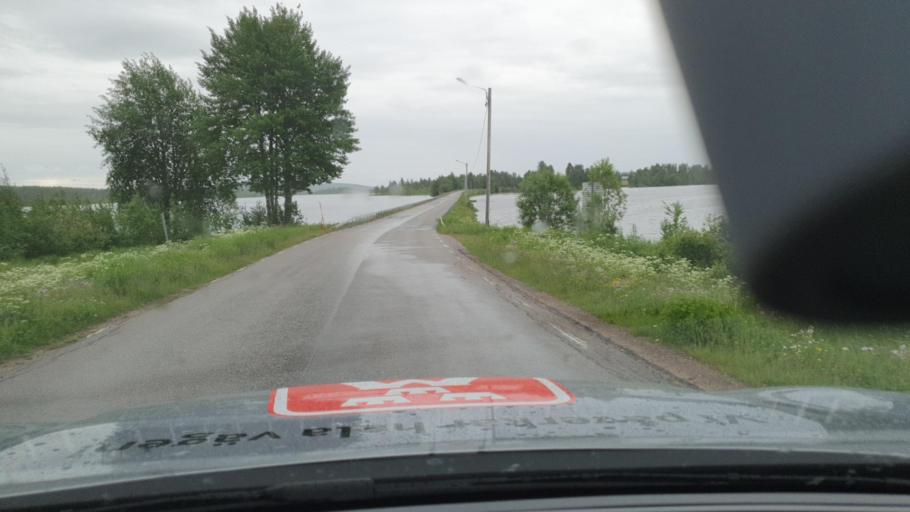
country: SE
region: Norrbotten
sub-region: Pajala Kommun
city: Pajala
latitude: 66.8038
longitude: 23.1202
